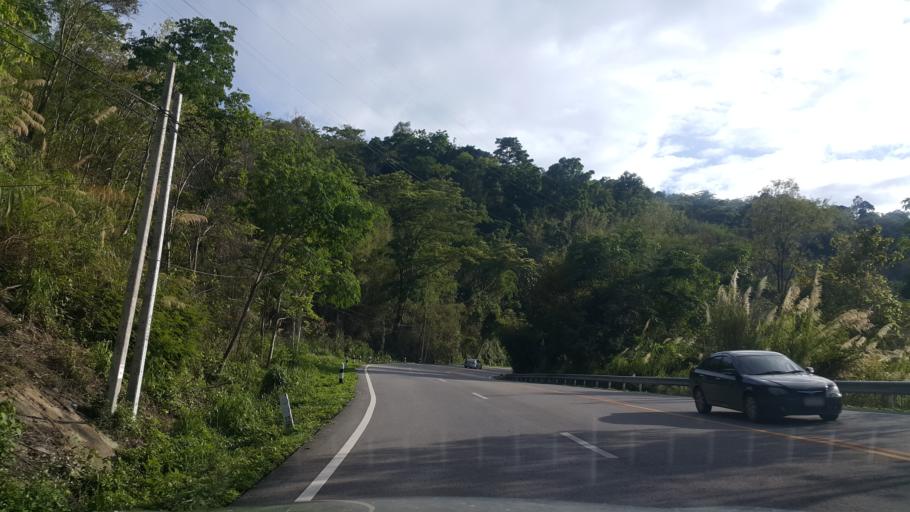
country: TH
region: Phayao
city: Phayao
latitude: 19.0611
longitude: 99.8002
